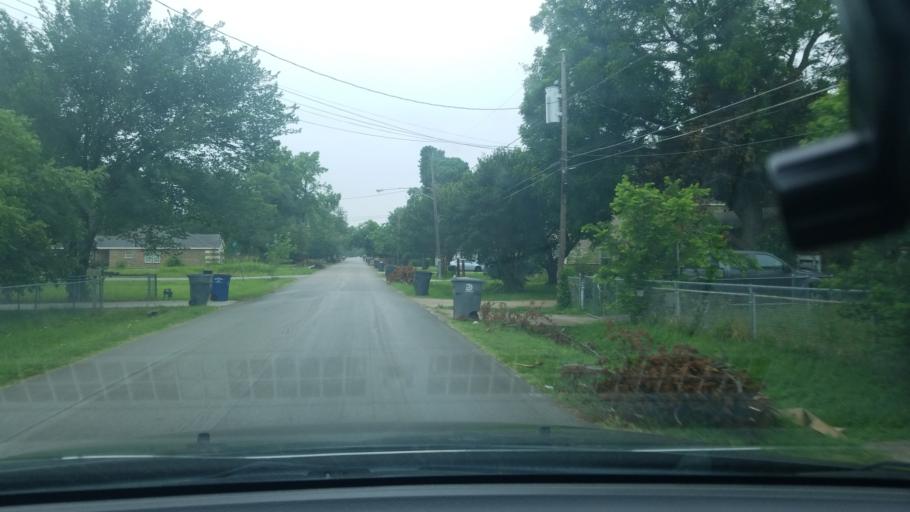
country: US
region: Texas
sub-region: Dallas County
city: Balch Springs
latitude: 32.7532
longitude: -96.6801
